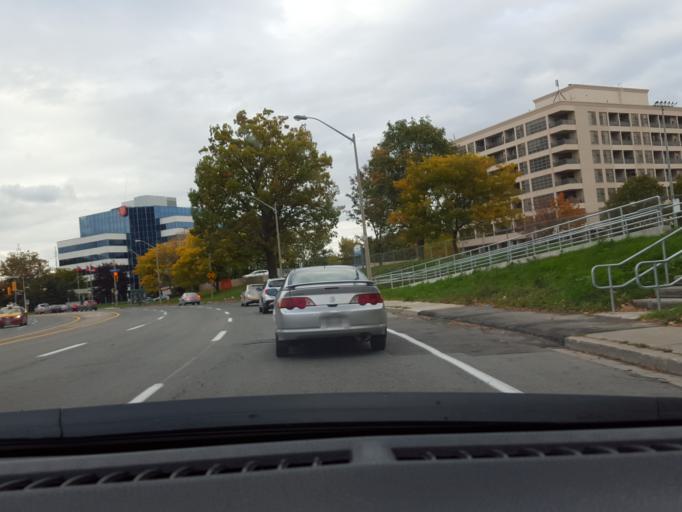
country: CA
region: Ontario
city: Toronto
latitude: 43.7010
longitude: -79.3514
